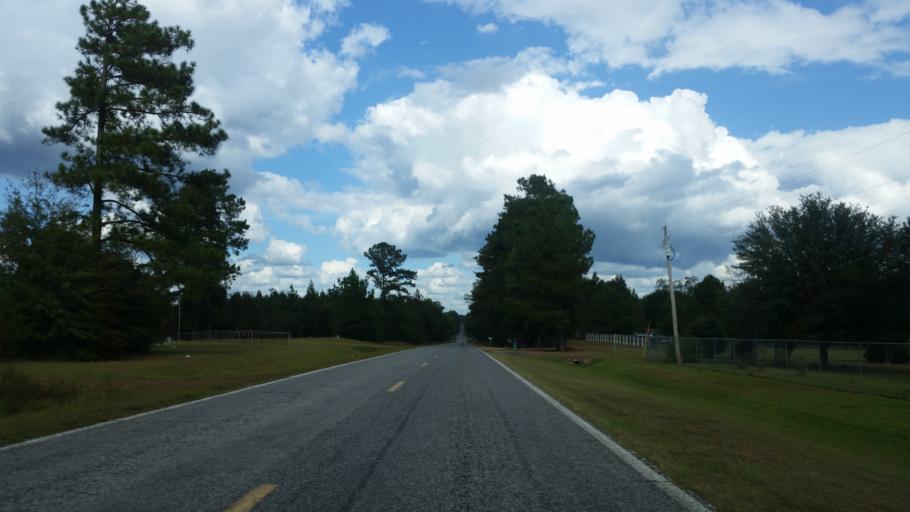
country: US
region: Mississippi
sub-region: Stone County
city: Wiggins
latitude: 30.9148
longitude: -89.0815
